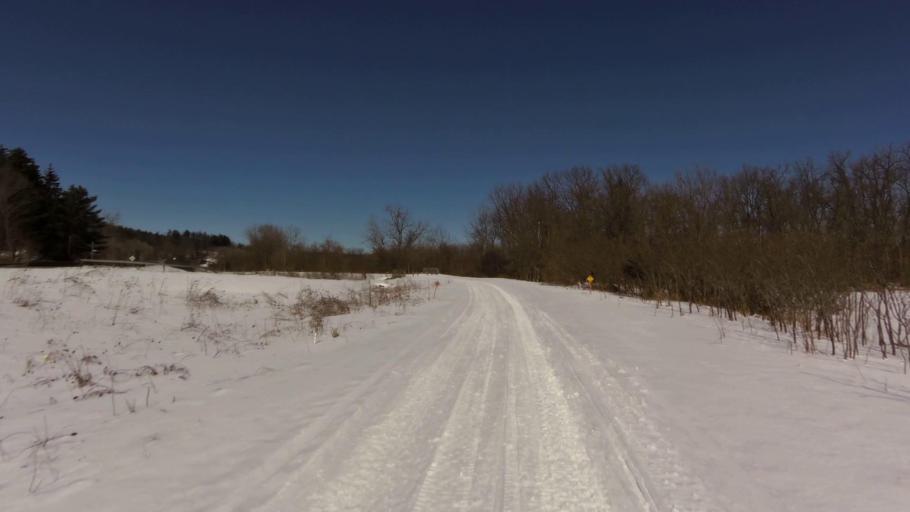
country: US
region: New York
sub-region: Allegany County
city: Houghton
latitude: 42.3717
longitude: -78.1408
